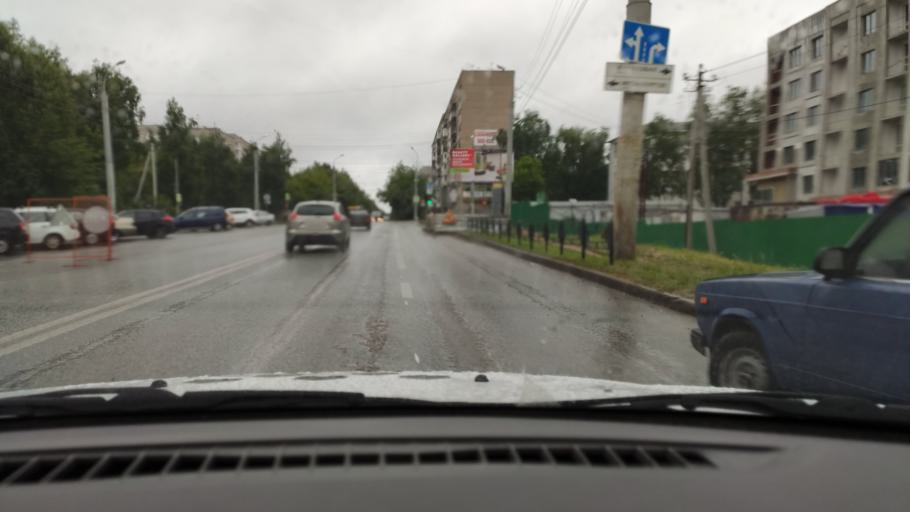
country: RU
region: Udmurtiya
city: Izhevsk
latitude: 56.8768
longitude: 53.1954
